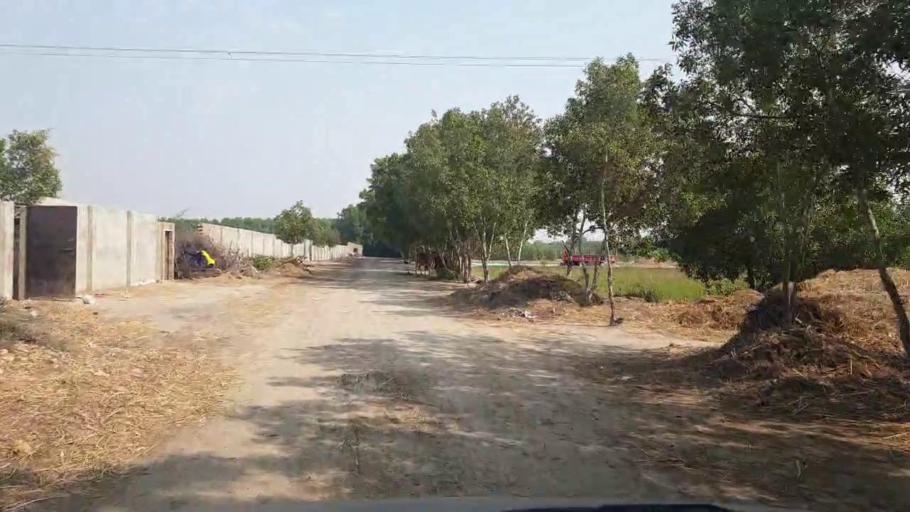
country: PK
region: Sindh
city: Tando Muhammad Khan
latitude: 25.0275
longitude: 68.3949
